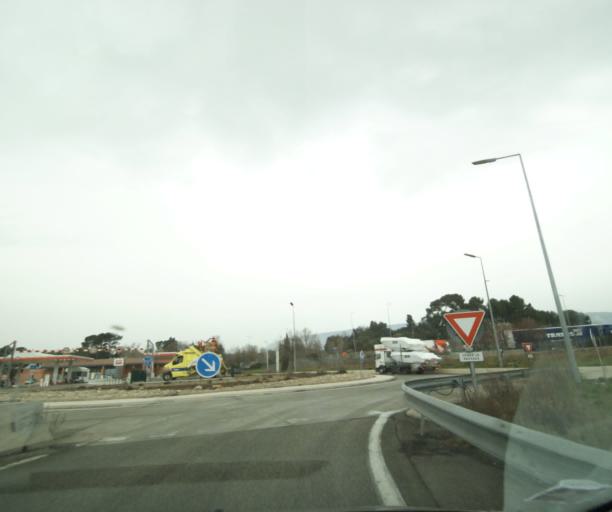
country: FR
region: Provence-Alpes-Cote d'Azur
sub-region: Departement des Bouches-du-Rhone
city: Peynier
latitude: 43.4709
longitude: 5.6453
